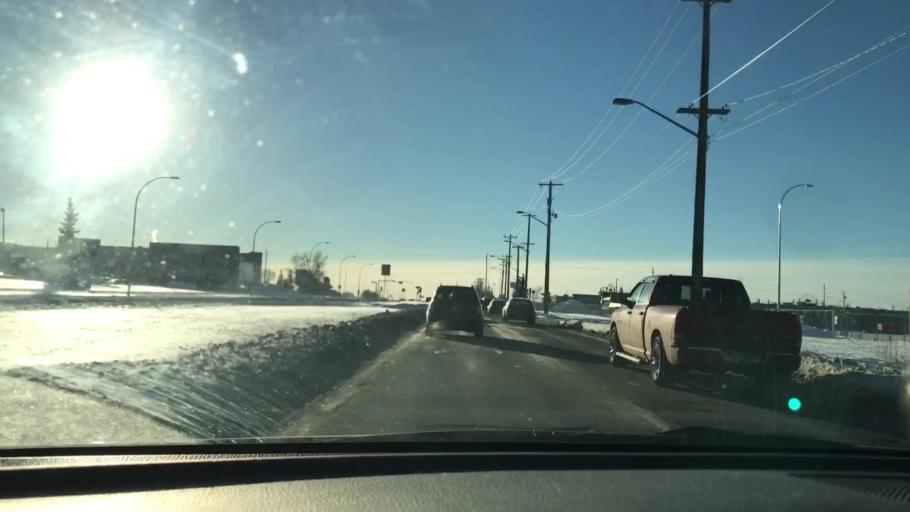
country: CA
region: Alberta
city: Edmonton
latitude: 53.4907
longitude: -113.4673
